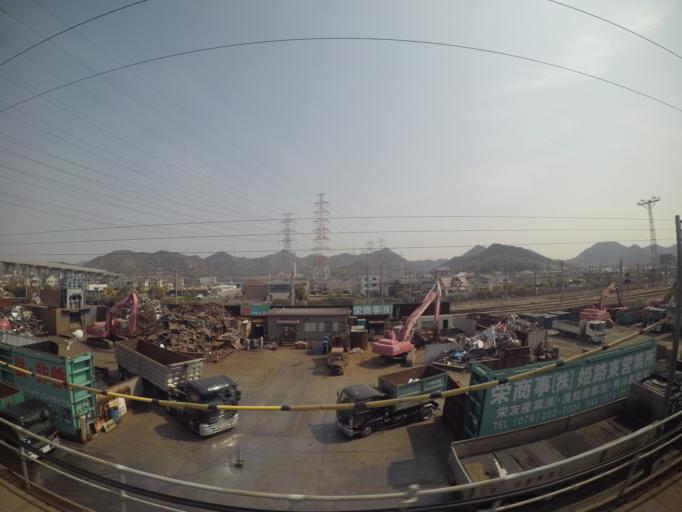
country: JP
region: Hyogo
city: Shirahamacho-usazakiminami
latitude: 34.8091
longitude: 134.7465
